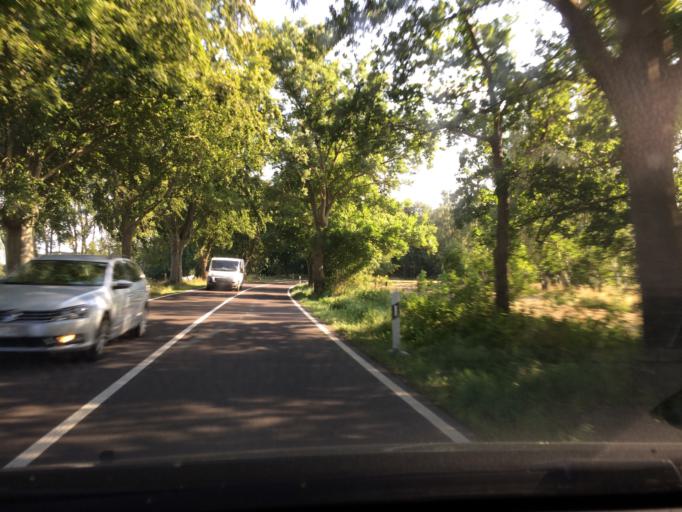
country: DE
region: Mecklenburg-Vorpommern
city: Ostseebad Binz
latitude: 54.4190
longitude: 13.5425
